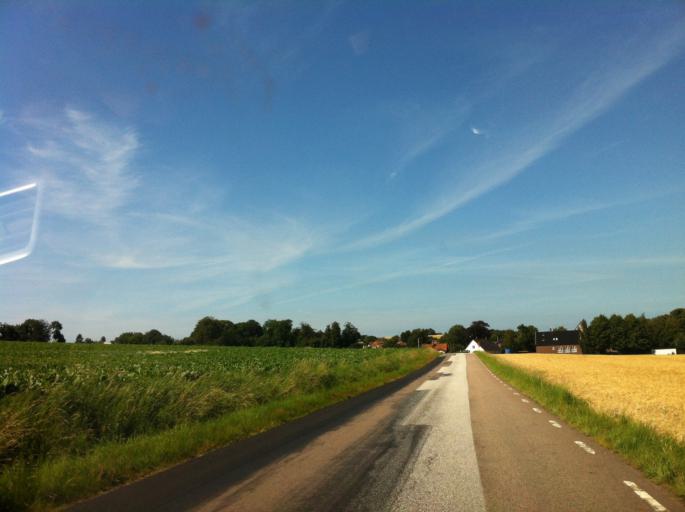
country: SE
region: Skane
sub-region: Landskrona
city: Asmundtorp
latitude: 55.9285
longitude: 12.8886
